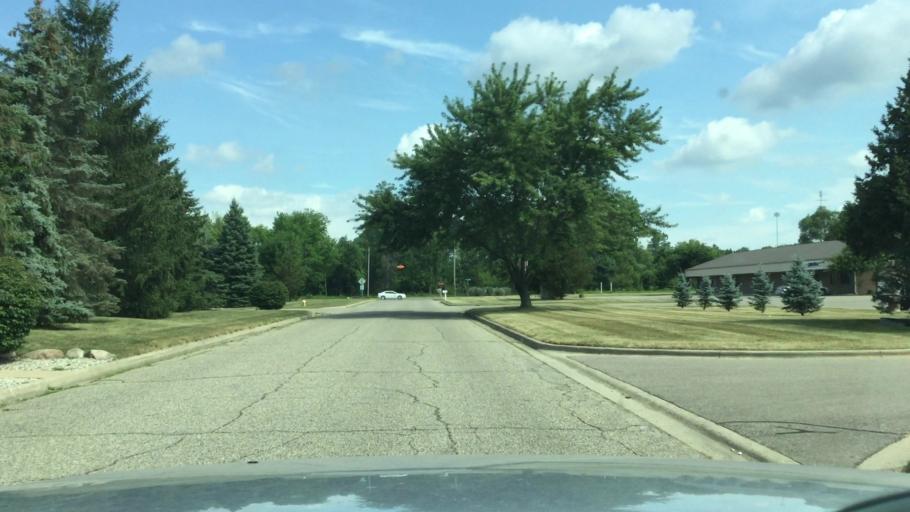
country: US
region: Michigan
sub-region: Genesee County
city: Flushing
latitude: 43.0588
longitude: -83.7885
